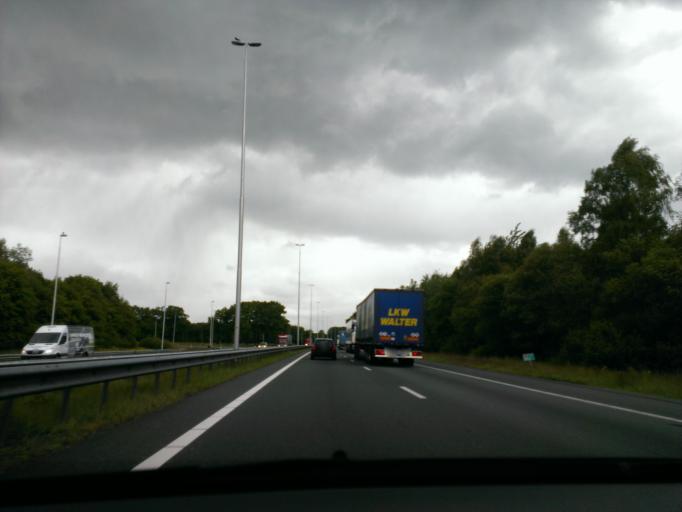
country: NL
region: Gelderland
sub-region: Gemeente Nijmegen
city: Lindenholt
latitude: 51.7986
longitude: 5.7960
